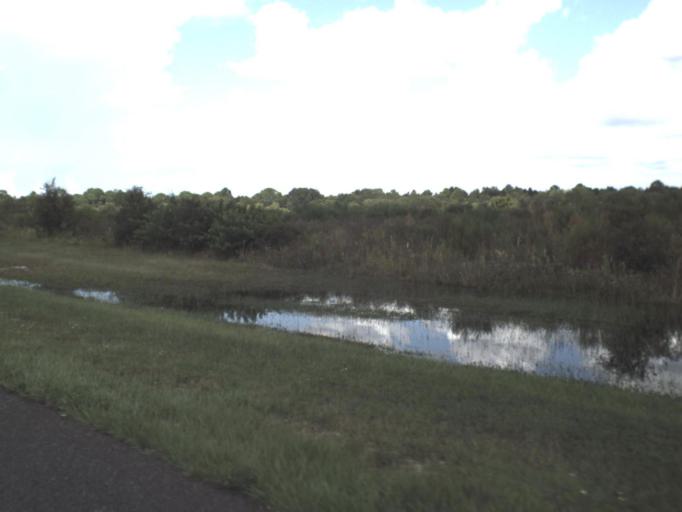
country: US
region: Florida
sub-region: Sarasota County
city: Plantation
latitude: 27.0497
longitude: -82.3232
